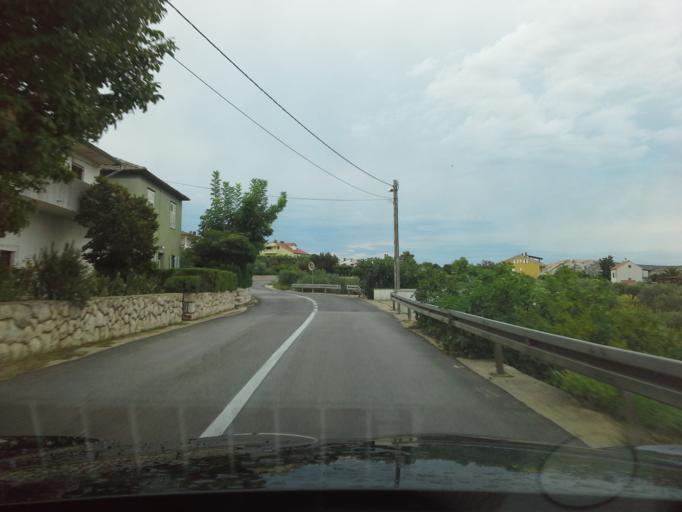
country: HR
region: Primorsko-Goranska
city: Banjol
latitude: 44.7304
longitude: 14.8133
